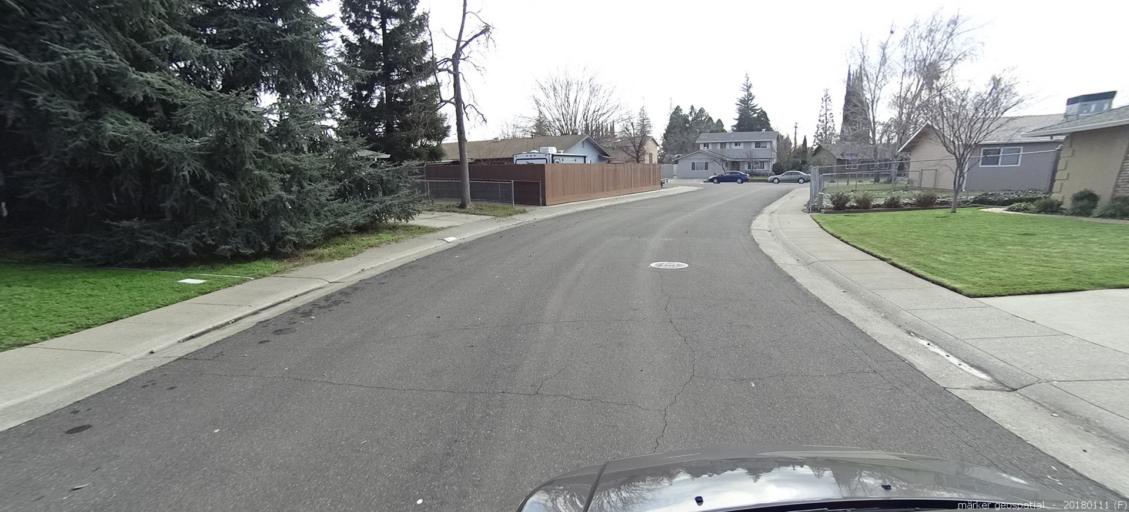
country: US
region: California
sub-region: Sacramento County
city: Rancho Cordova
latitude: 38.6152
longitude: -121.2934
